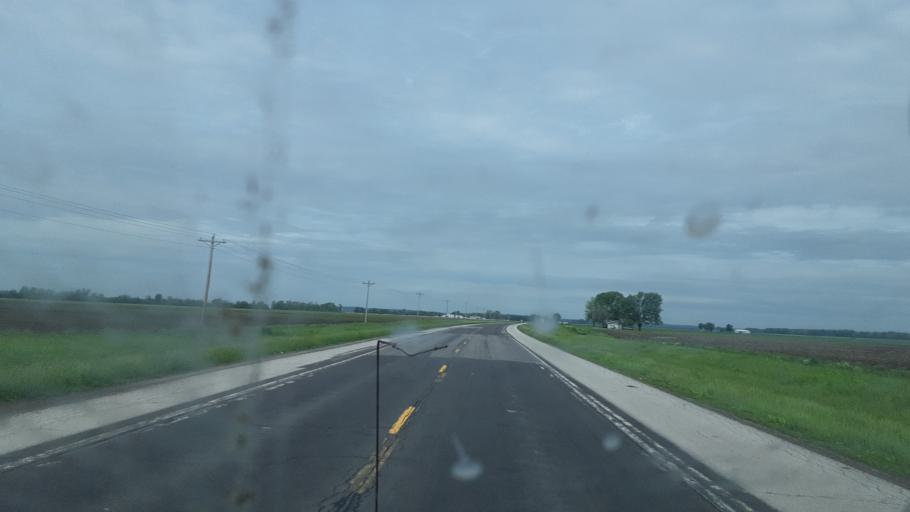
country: US
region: Illinois
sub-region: Hancock County
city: Warsaw
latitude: 40.3757
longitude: -91.4888
